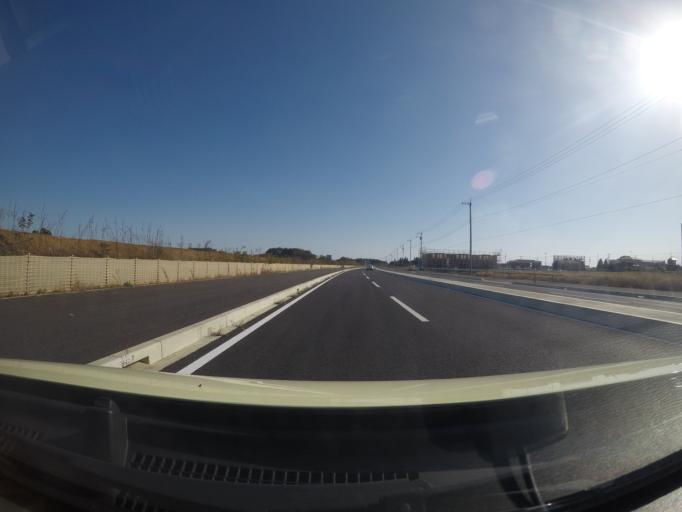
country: JP
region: Ibaraki
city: Naka
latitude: 36.1036
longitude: 140.1243
